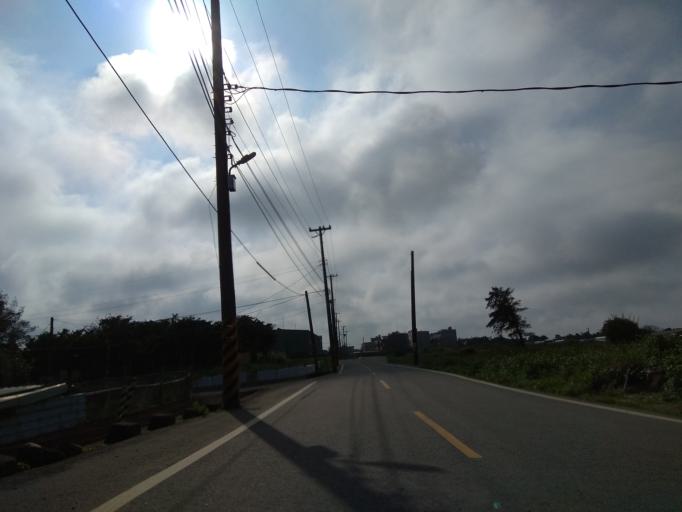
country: TW
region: Taiwan
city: Taoyuan City
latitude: 25.0697
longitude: 121.1606
